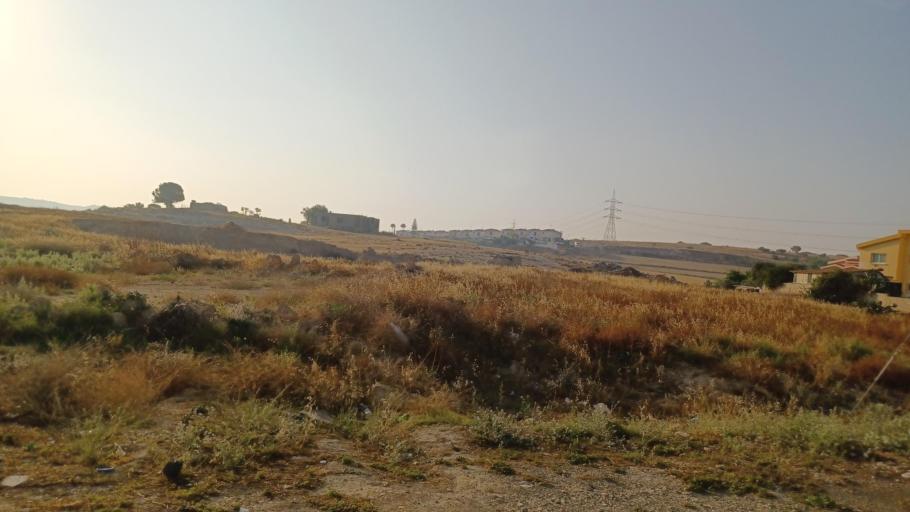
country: CY
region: Larnaka
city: Pyla
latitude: 35.0052
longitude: 33.6916
